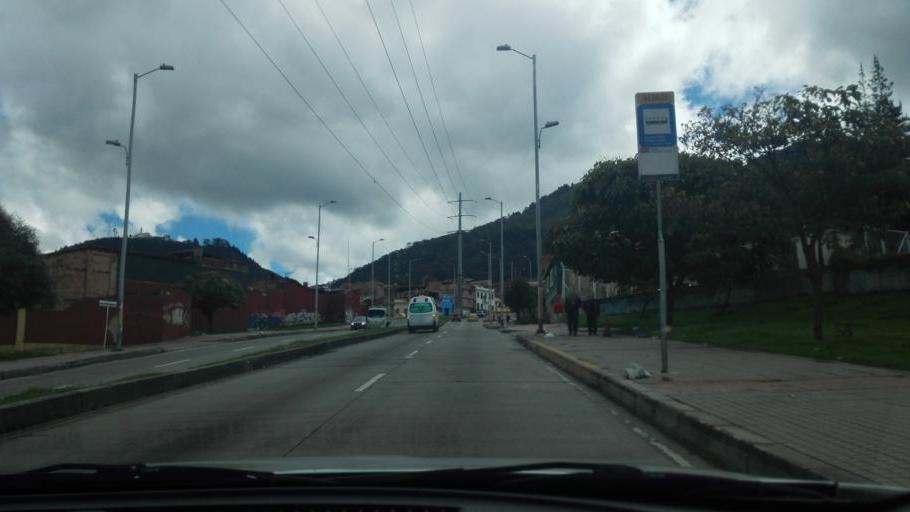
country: CO
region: Bogota D.C.
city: Bogota
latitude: 4.5898
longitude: -74.0750
